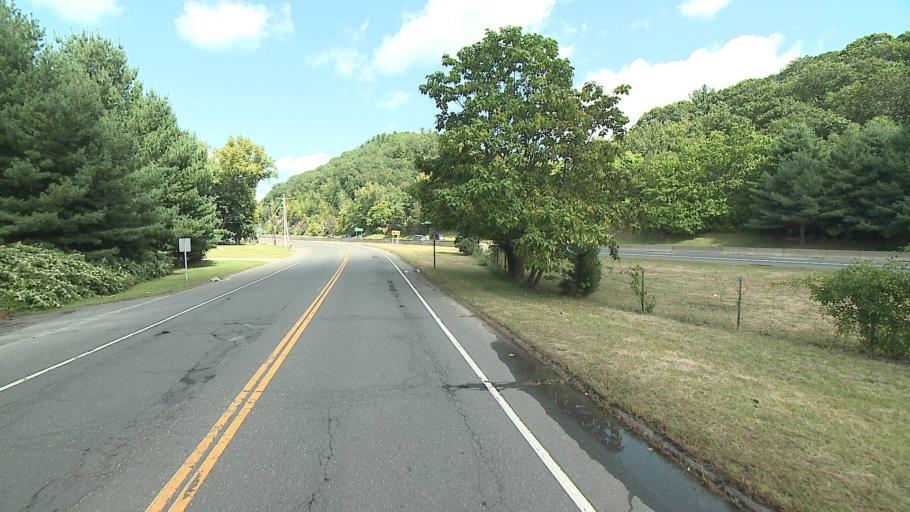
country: US
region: Connecticut
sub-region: New Haven County
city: Seymour
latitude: 41.4087
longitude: -73.0705
